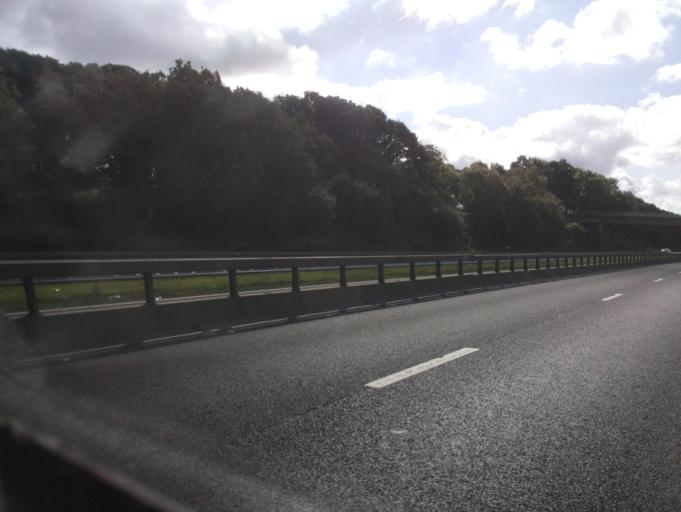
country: GB
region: England
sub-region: Cumbria
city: Milnthorpe
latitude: 54.2564
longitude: -2.6896
